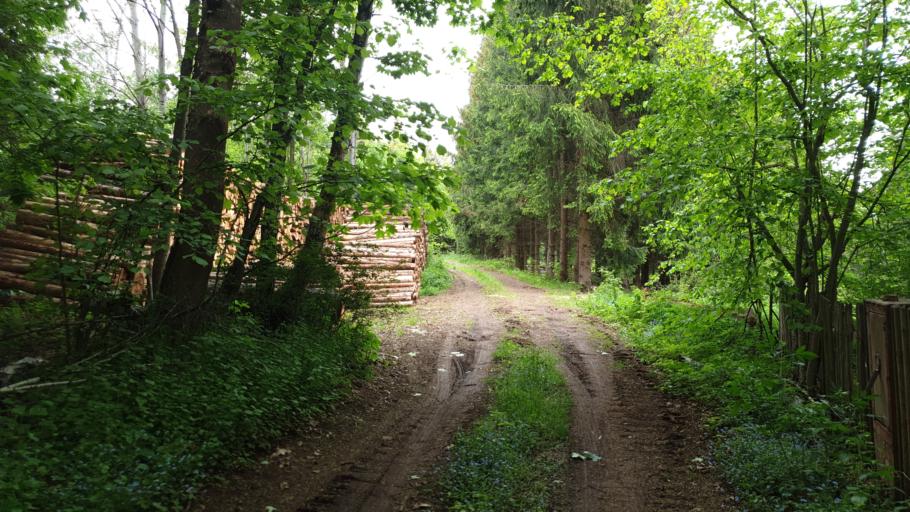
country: DE
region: Saxony
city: Barenstein
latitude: 50.8025
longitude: 13.7793
